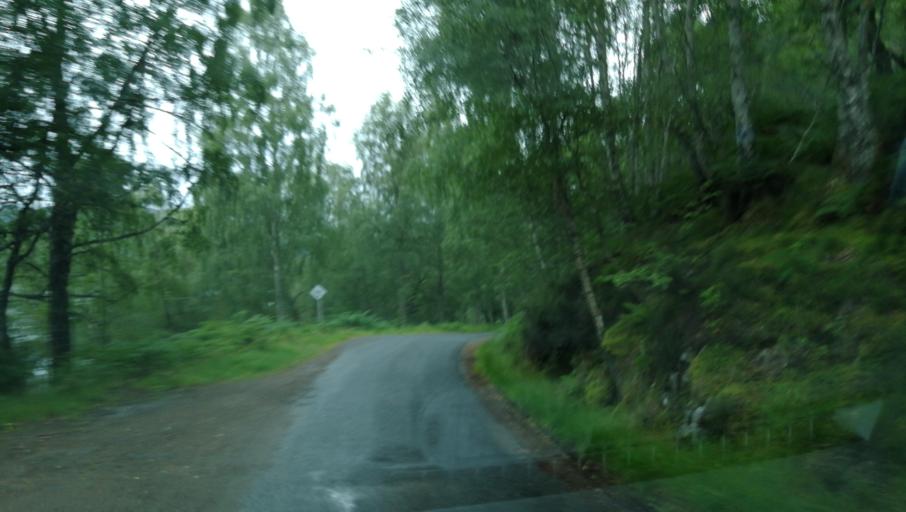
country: GB
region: Scotland
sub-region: Highland
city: Spean Bridge
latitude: 57.2848
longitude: -4.9235
